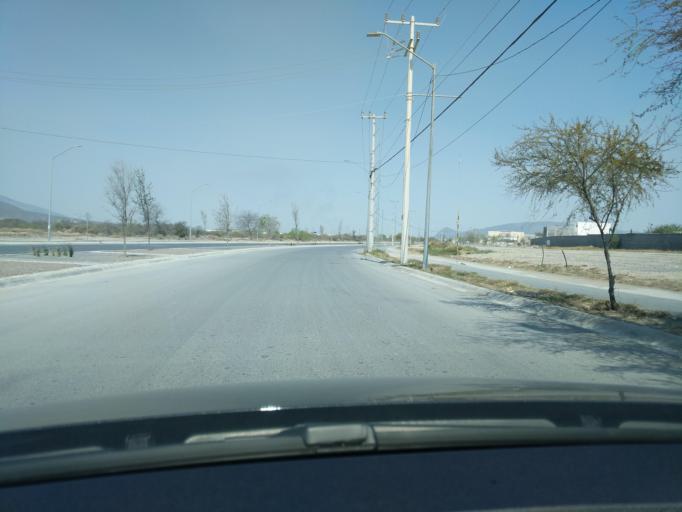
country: MX
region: Nuevo Leon
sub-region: Garcia
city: Los Parques
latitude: 25.7814
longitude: -100.4970
